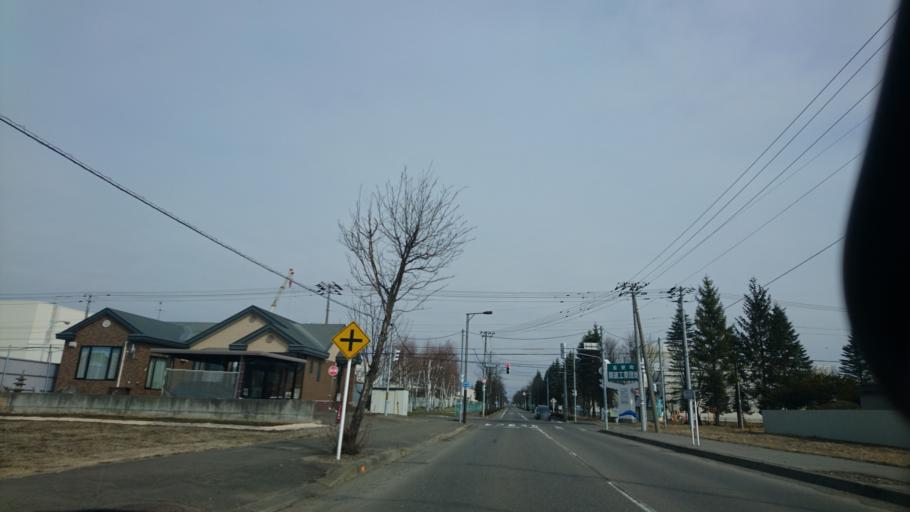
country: JP
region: Hokkaido
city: Otofuke
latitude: 42.9773
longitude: 143.2118
